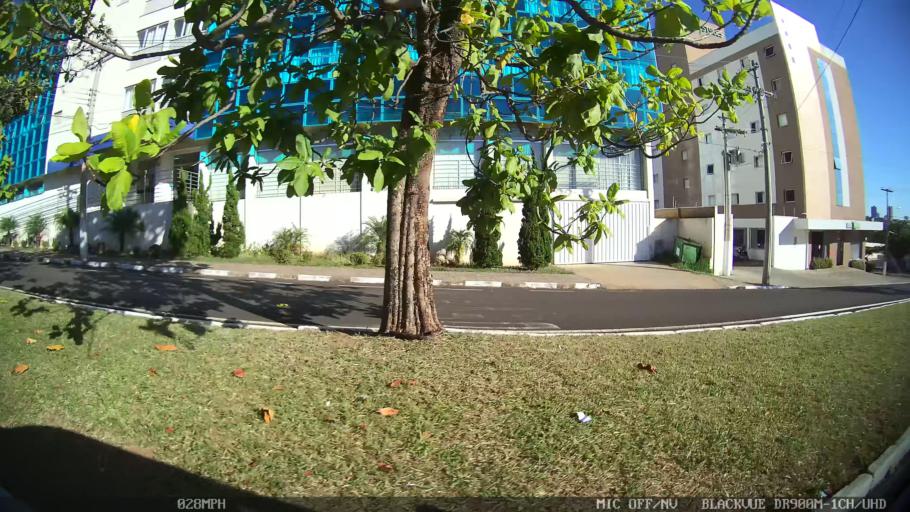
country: BR
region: Sao Paulo
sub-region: Franca
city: Franca
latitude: -20.5558
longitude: -47.4076
